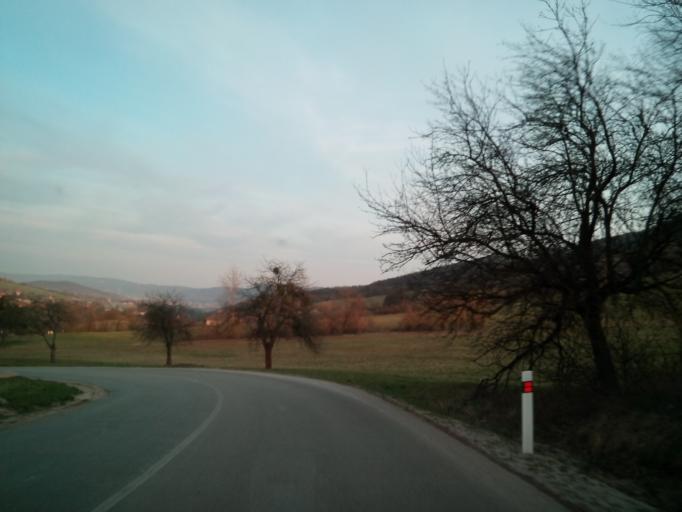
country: SK
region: Kosicky
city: Roznava
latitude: 48.6668
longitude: 20.4255
